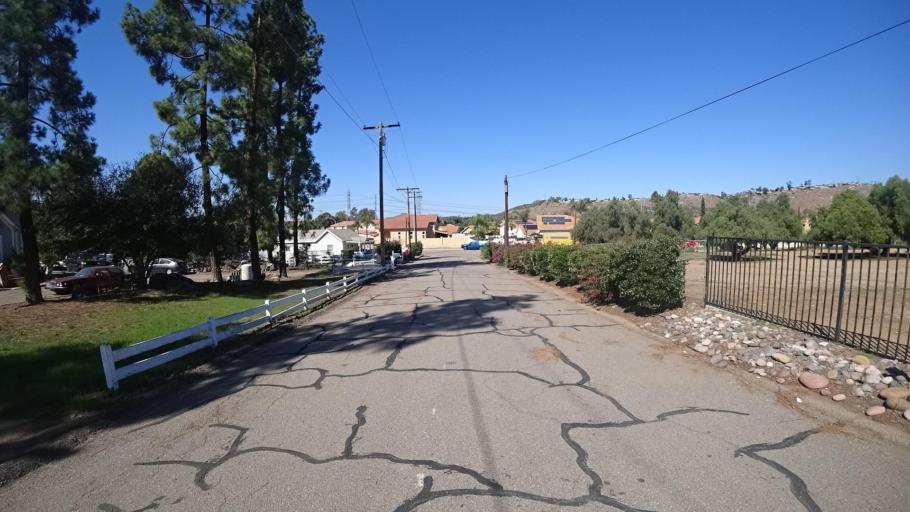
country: US
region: California
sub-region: San Diego County
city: Rancho San Diego
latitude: 32.7416
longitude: -116.9099
